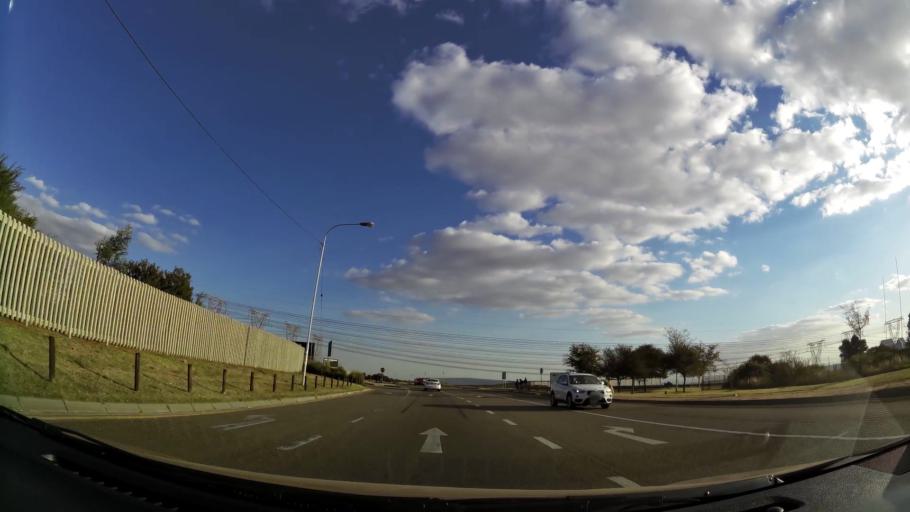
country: ZA
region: Gauteng
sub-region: City of Tshwane Metropolitan Municipality
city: Centurion
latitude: -25.9236
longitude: 28.1586
